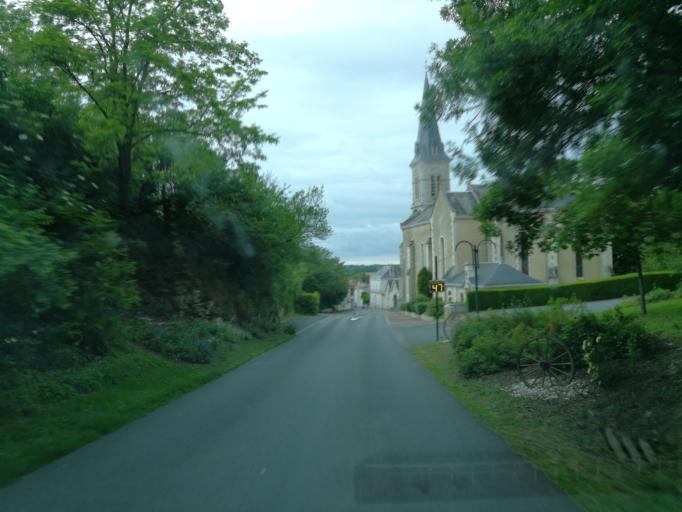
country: FR
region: Pays de la Loire
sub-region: Departement de la Vendee
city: Vix
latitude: 46.3722
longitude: -0.9173
